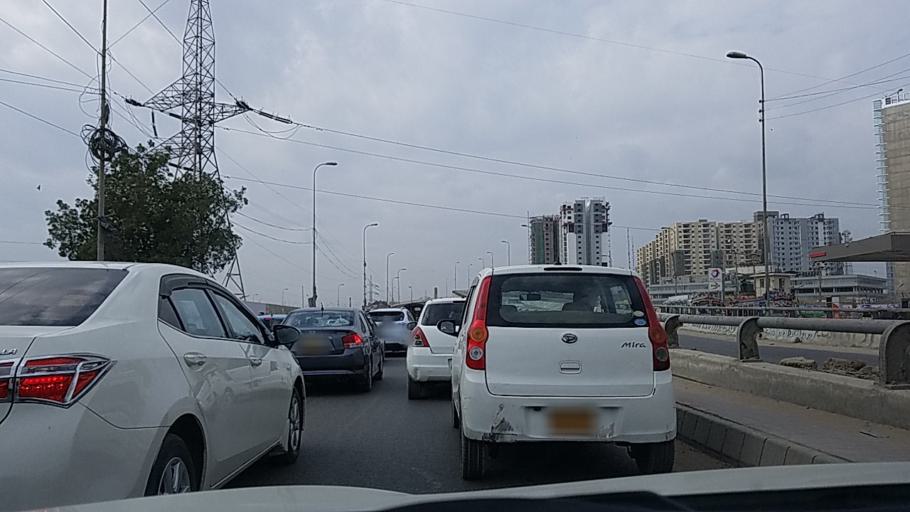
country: PK
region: Sindh
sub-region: Karachi District
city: Karachi
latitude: 24.8287
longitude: 67.0825
